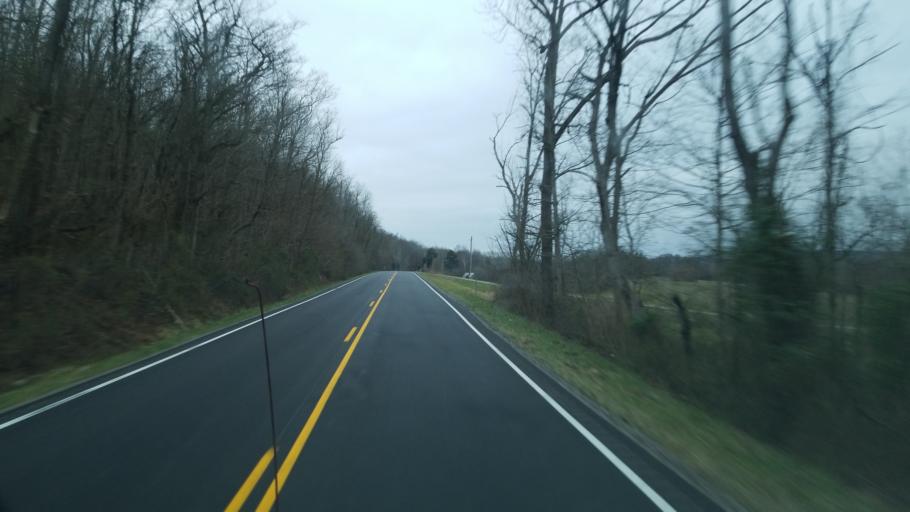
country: US
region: Kentucky
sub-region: Bracken County
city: Augusta
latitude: 38.7789
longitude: -83.9531
